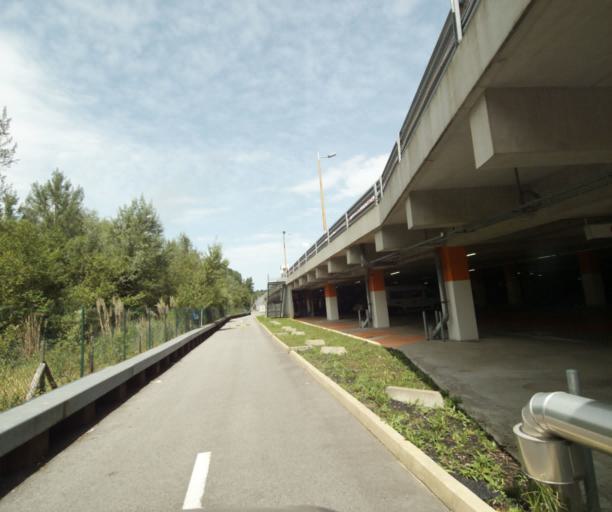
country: FR
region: Aquitaine
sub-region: Departement des Pyrenees-Atlantiques
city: Mouguerre
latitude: 43.4798
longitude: -1.4462
